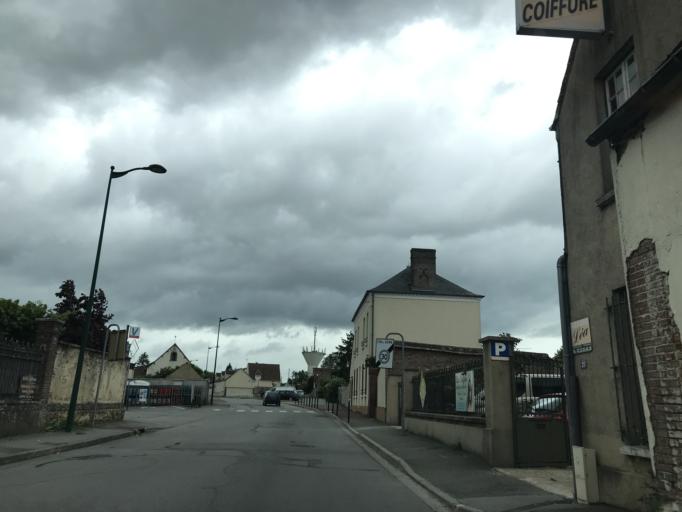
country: FR
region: Haute-Normandie
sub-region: Departement de l'Eure
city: La Couture-Boussey
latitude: 48.8988
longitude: 1.4052
